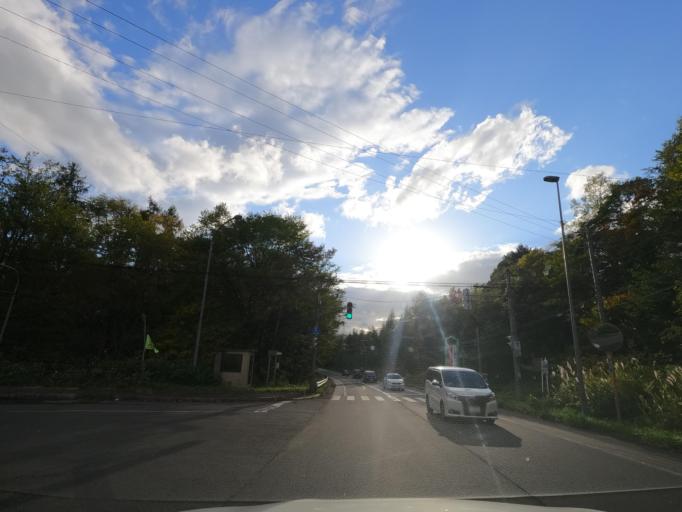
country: JP
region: Hokkaido
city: Date
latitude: 42.6500
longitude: 141.0603
